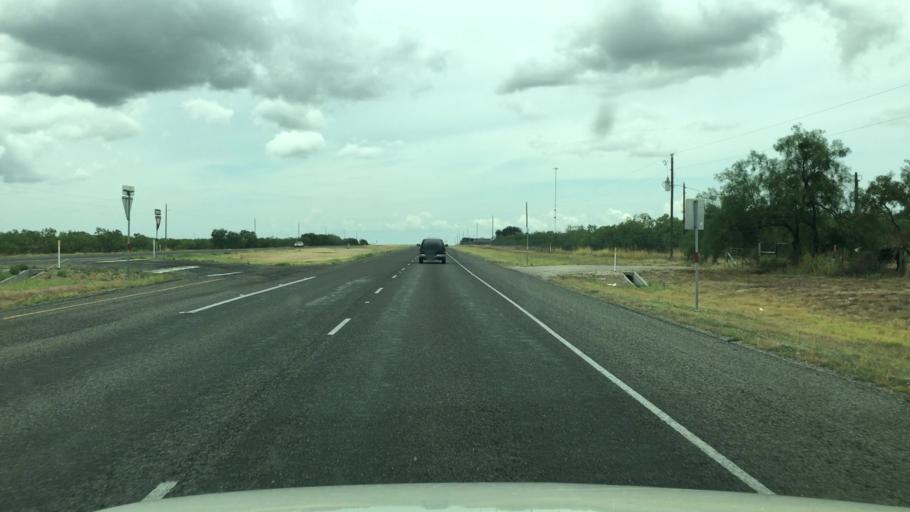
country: US
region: Texas
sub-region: Concho County
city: Eden
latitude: 31.2219
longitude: -99.9709
